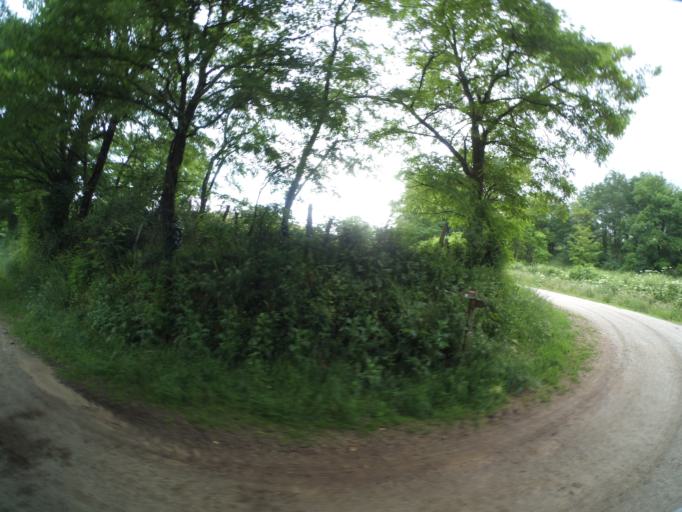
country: FR
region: Pays de la Loire
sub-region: Departement de la Vendee
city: Nesmy
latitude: 46.6059
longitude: -1.3774
